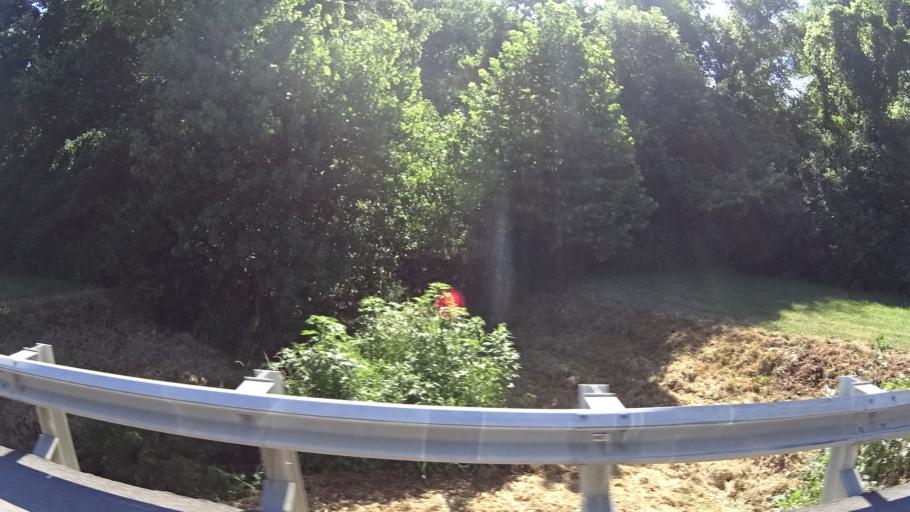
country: US
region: Ohio
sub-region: Erie County
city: Sandusky
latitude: 41.3652
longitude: -82.7279
